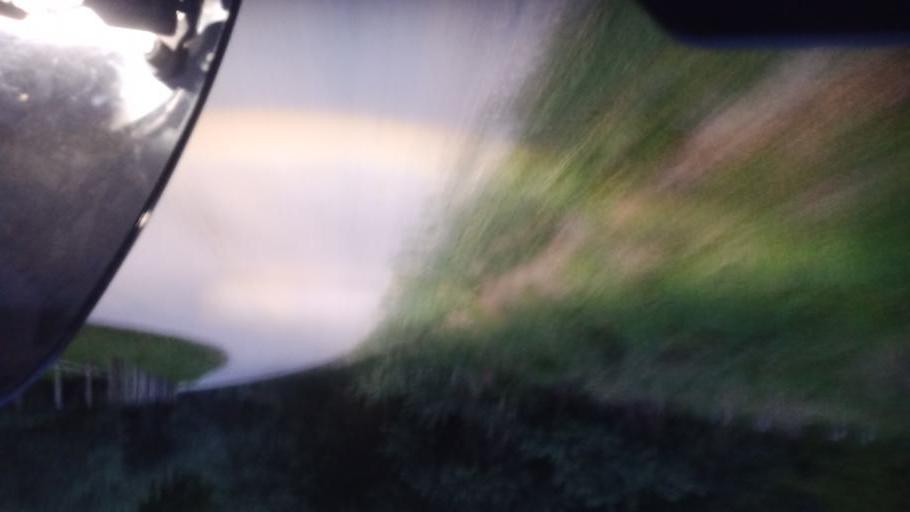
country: NZ
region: Gisborne
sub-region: Gisborne District
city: Gisborne
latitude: -38.4933
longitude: 177.9606
